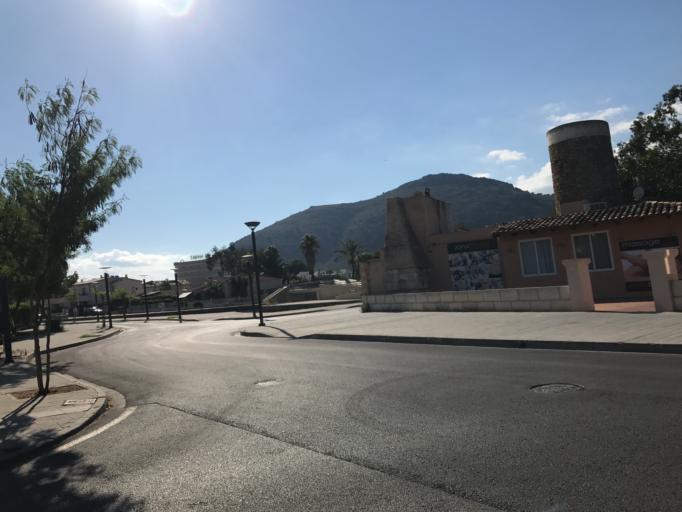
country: ES
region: Balearic Islands
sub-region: Illes Balears
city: Alcudia
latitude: 39.8357
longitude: 3.1130
